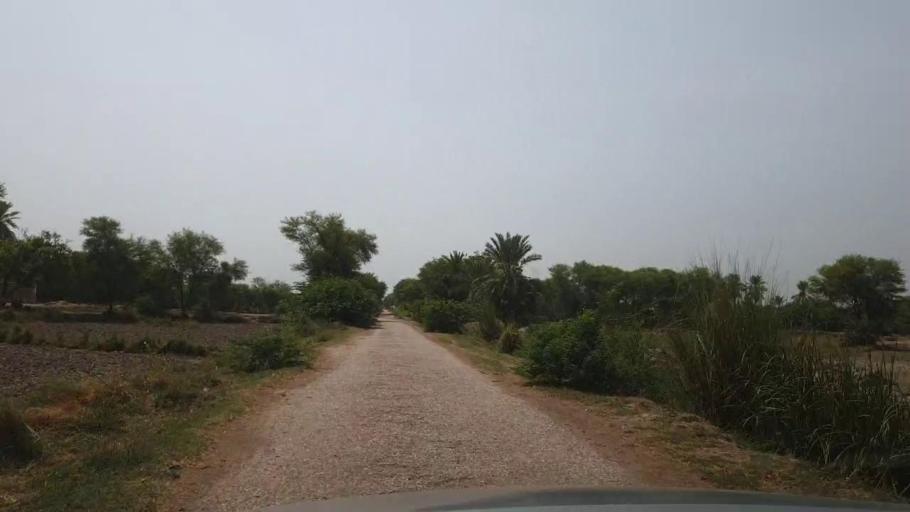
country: PK
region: Sindh
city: Madeji
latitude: 27.8266
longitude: 68.4327
